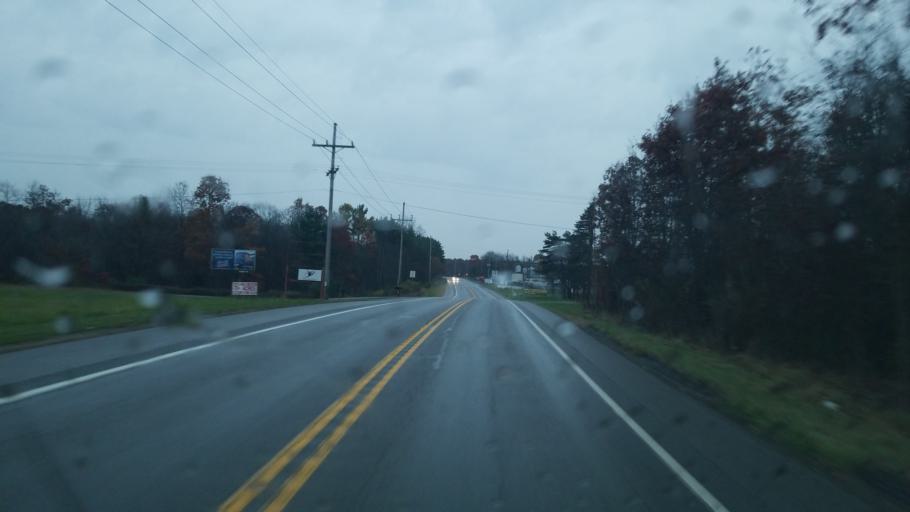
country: US
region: Pennsylvania
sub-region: Clarion County
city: Marianne
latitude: 41.2257
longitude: -79.4329
